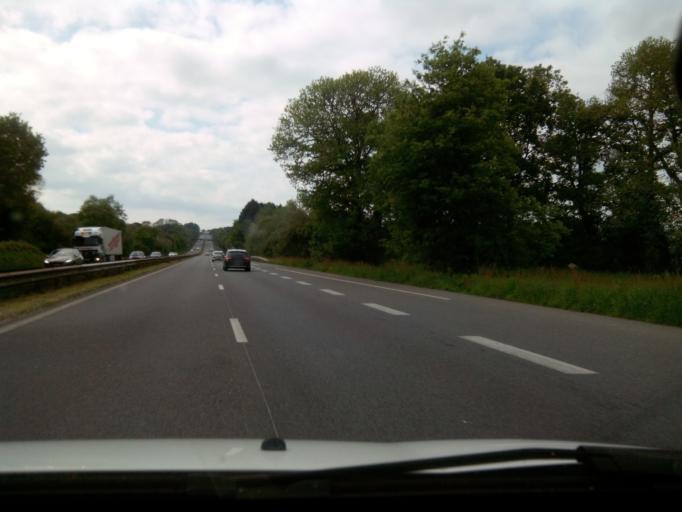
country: FR
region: Brittany
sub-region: Departement des Cotes-d'Armor
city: Graces
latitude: 48.5533
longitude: -3.1722
